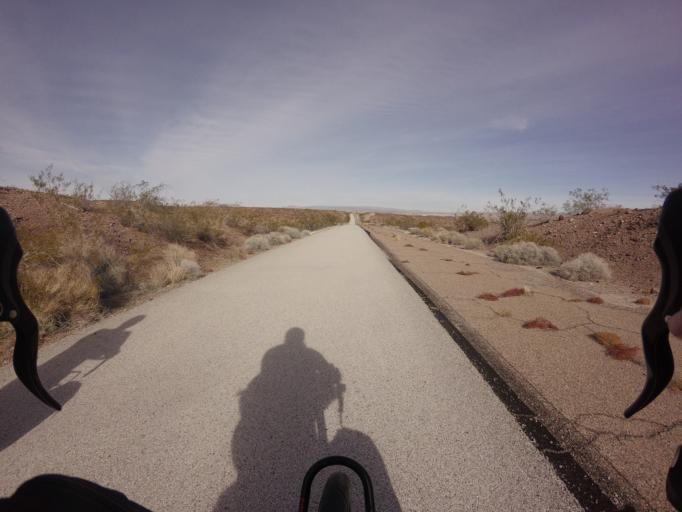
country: US
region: Nevada
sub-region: Clark County
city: Boulder City
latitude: 36.0930
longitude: -114.8418
